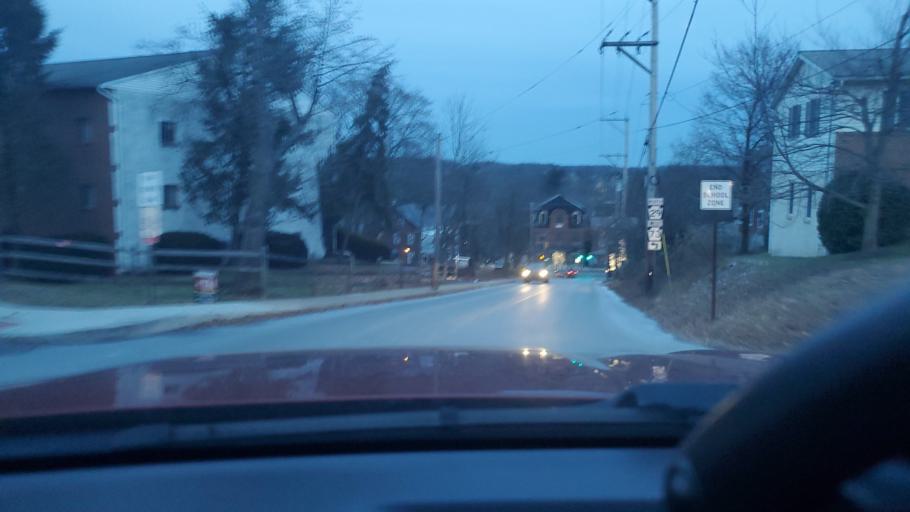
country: US
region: Pennsylvania
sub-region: Montgomery County
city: Schwenksville
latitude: 40.2519
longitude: -75.4648
